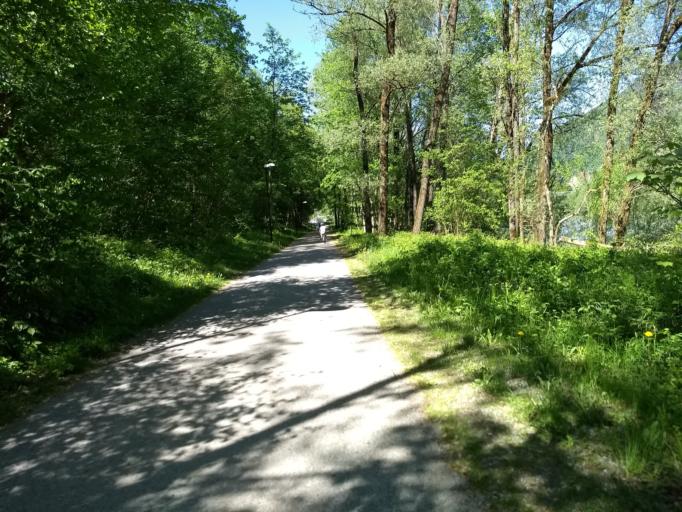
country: AT
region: Salzburg
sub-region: Politischer Bezirk Salzburg-Umgebung
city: Elsbethen
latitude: 47.7799
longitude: 13.0753
